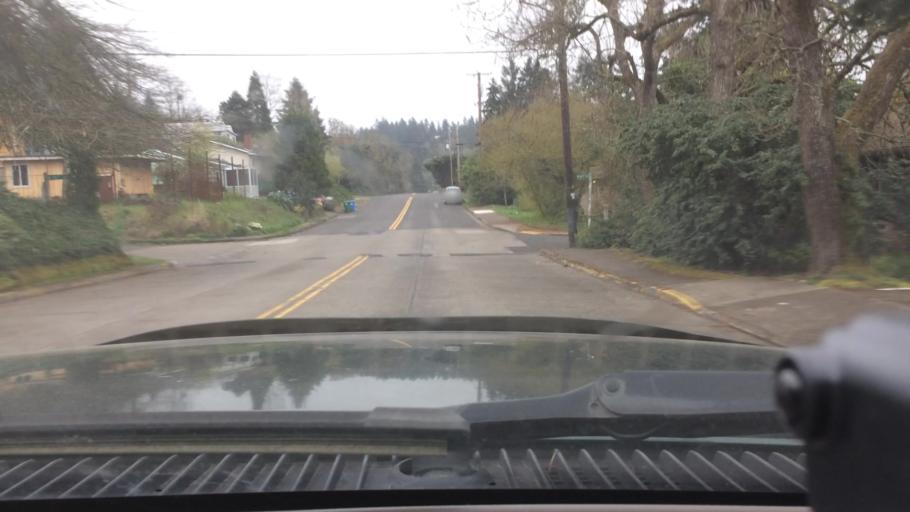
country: US
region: Oregon
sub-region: Lane County
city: Eugene
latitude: 44.0318
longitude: -123.1013
